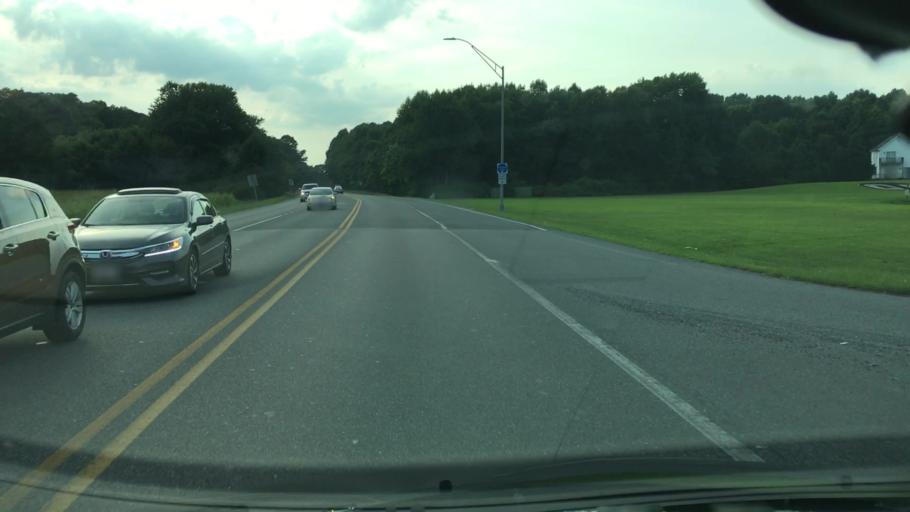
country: US
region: Maryland
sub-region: Worcester County
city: Ocean Pines
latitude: 38.3839
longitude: -75.1773
